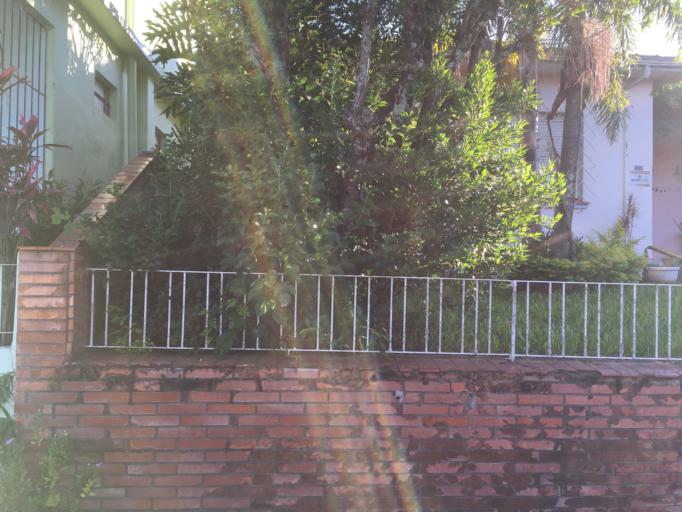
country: BR
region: Rio Grande do Sul
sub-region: Santa Maria
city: Santa Maria
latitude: -29.7000
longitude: -53.7088
